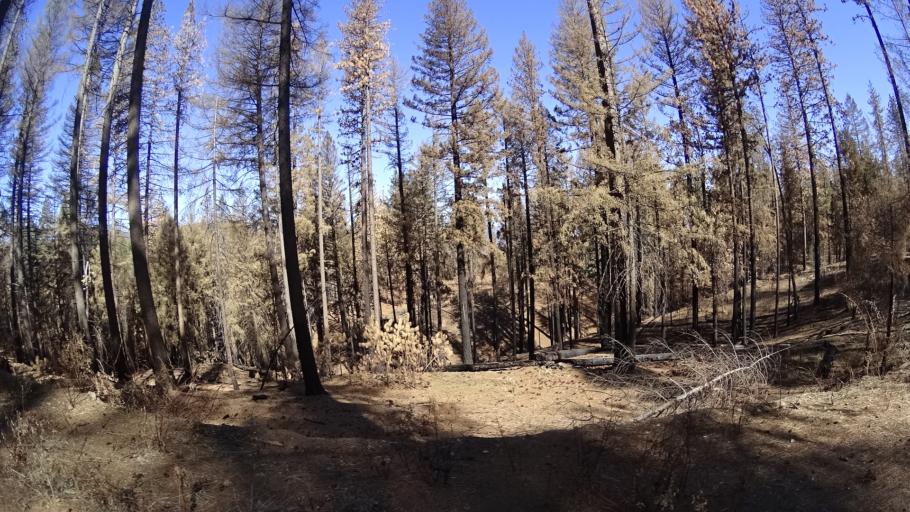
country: US
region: California
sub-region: Tehama County
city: Rancho Tehama Reserve
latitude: 39.6575
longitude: -122.7185
